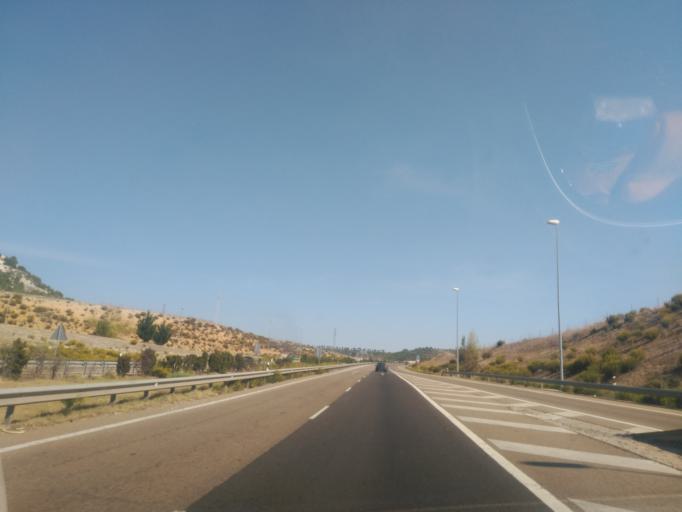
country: ES
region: Castille and Leon
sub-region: Provincia de Valladolid
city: Cisterniga
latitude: 41.6161
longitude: -4.6836
